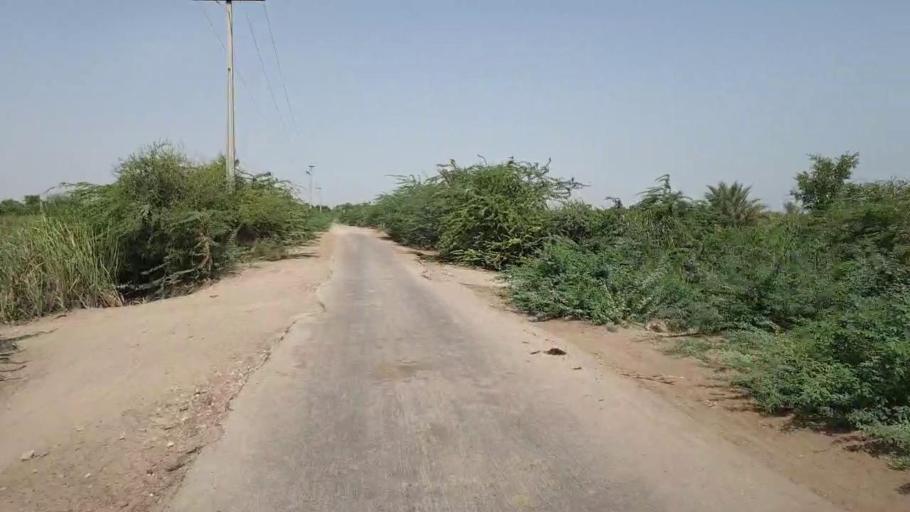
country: PK
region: Sindh
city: Jam Sahib
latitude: 26.4069
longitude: 68.8844
